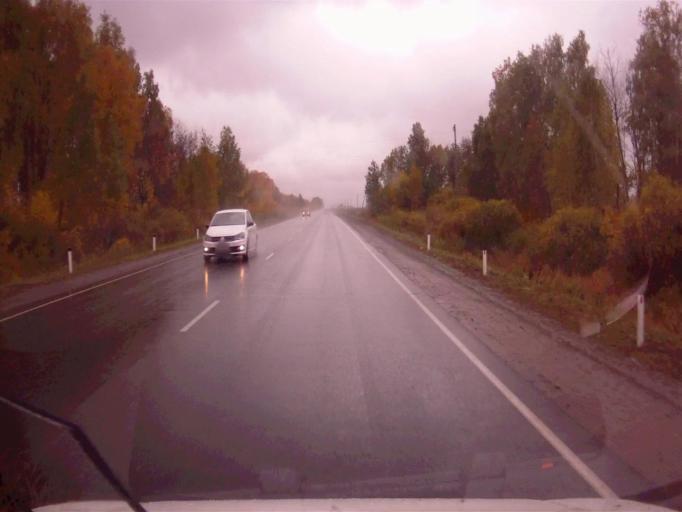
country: RU
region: Chelyabinsk
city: Argayash
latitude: 55.4241
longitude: 61.0076
